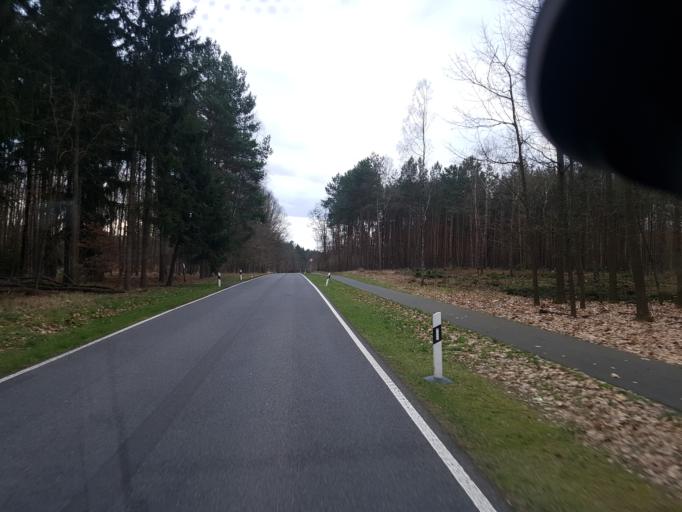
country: DE
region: Brandenburg
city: Gross Lindow
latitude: 52.1680
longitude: 14.4971
